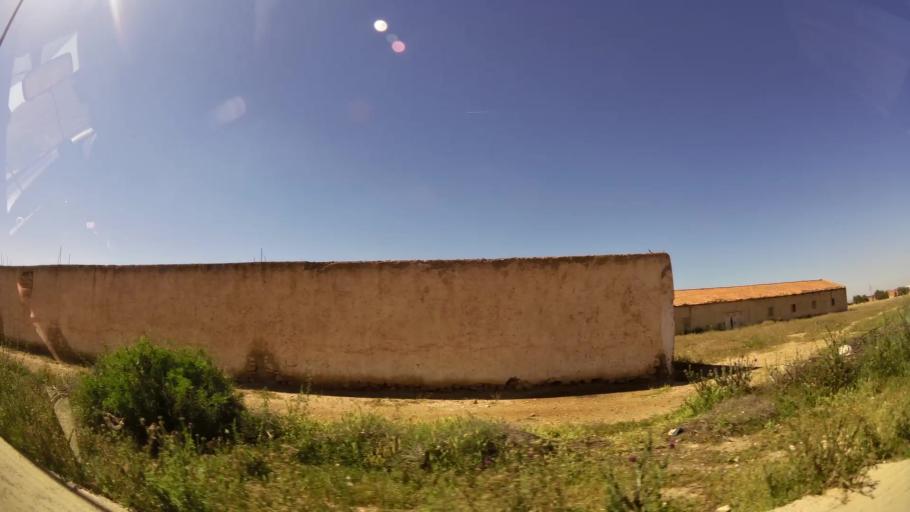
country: MA
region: Oriental
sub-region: Oujda-Angad
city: Oujda
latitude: 34.6932
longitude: -1.8639
